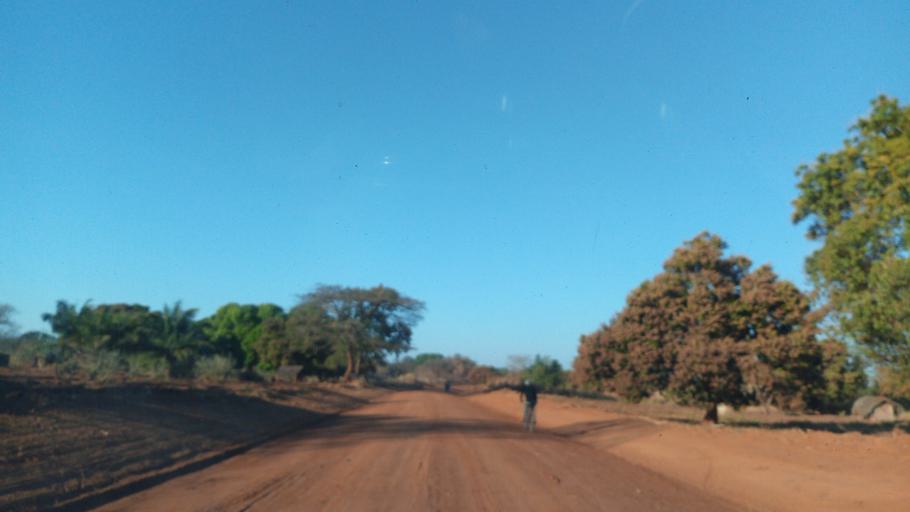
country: ZM
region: Luapula
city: Mwense
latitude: -10.4241
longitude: 28.6015
